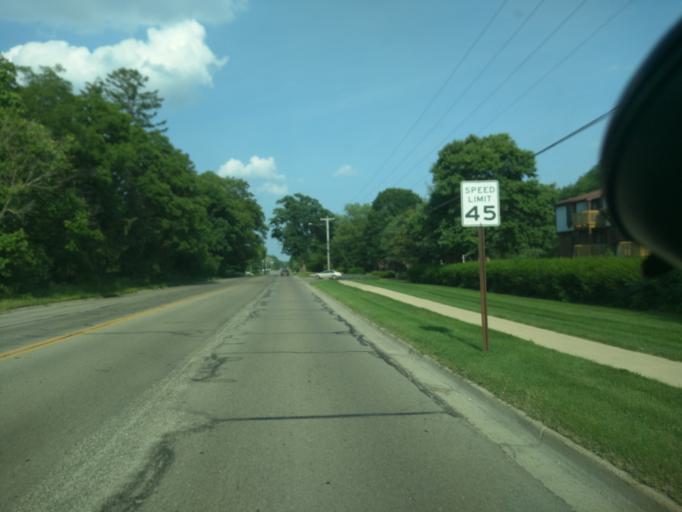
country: US
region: Michigan
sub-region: Jackson County
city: Jackson
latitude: 42.2765
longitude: -84.4476
